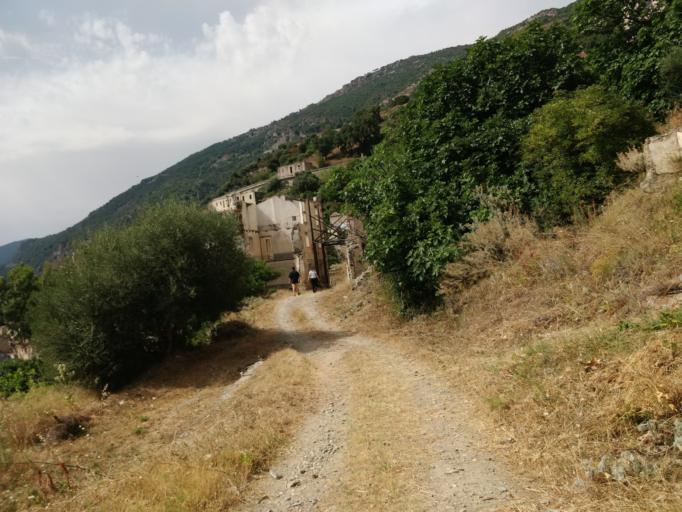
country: IT
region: Sardinia
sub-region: Provincia di Ogliastra
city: Gairo Sant'Elena
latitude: 39.8470
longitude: 9.4995
